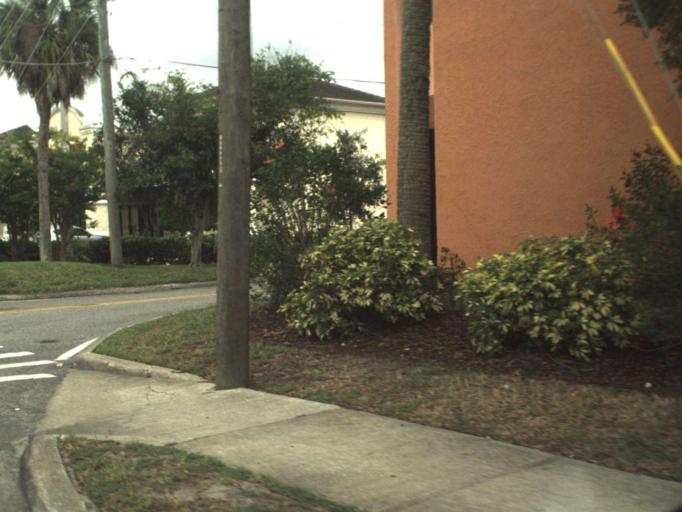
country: US
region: Florida
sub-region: Seminole County
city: Altamonte Springs
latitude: 28.6638
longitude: -81.3683
